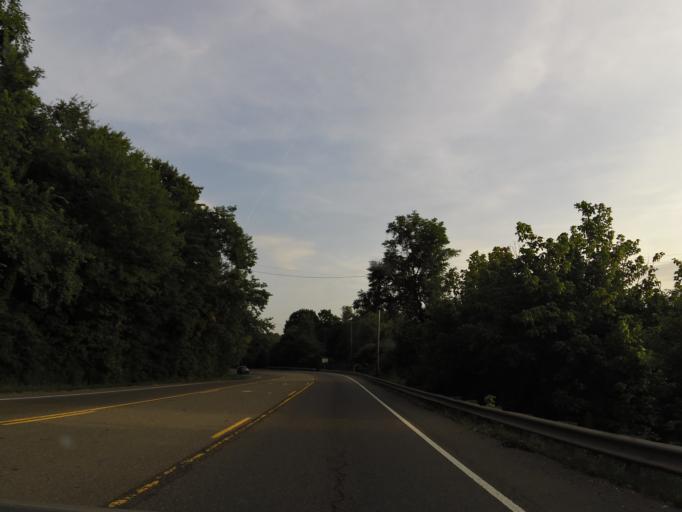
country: US
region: Tennessee
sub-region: Knox County
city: Mascot
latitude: 36.0149
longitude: -83.8264
